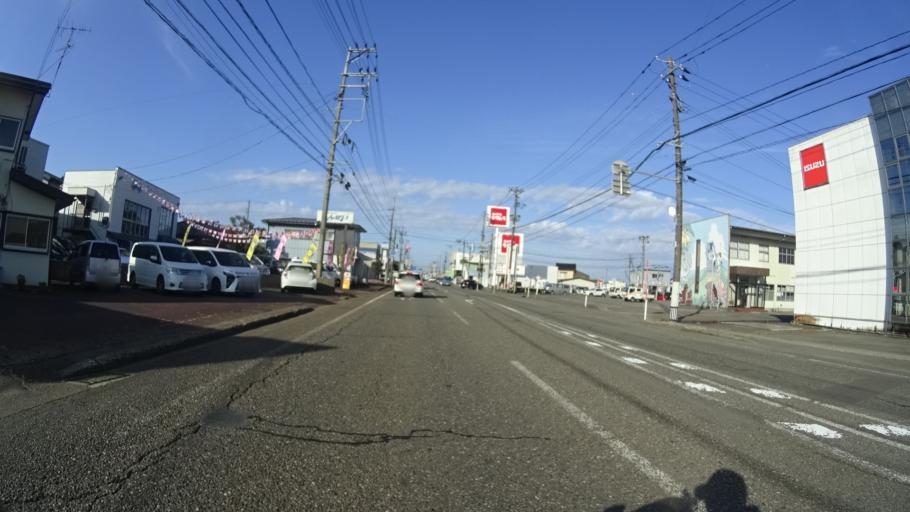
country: JP
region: Niigata
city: Joetsu
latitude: 37.1566
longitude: 138.2381
